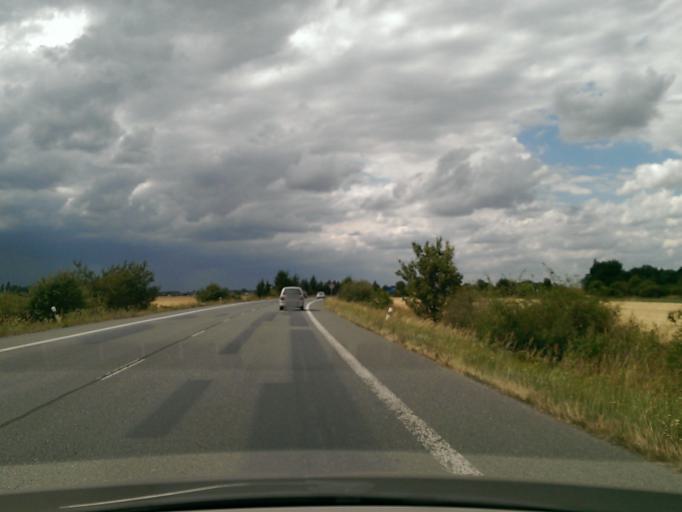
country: CZ
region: Central Bohemia
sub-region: Okres Nymburk
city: Podebrady
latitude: 50.1281
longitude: 15.1039
